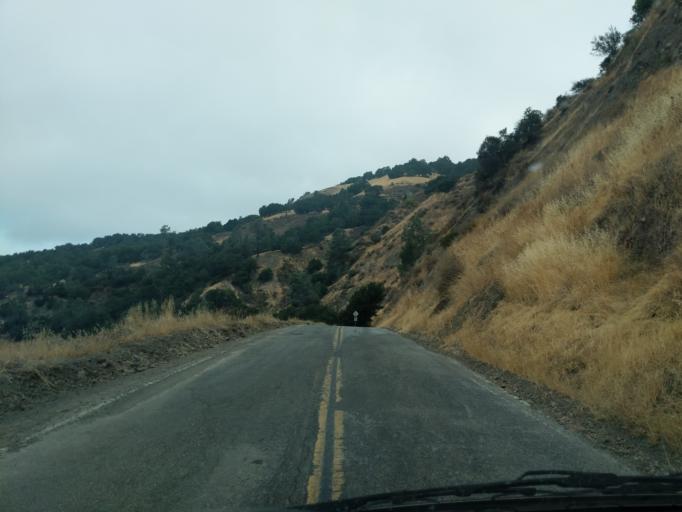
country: US
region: California
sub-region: Santa Clara County
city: San Martin
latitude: 37.1542
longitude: -121.5821
